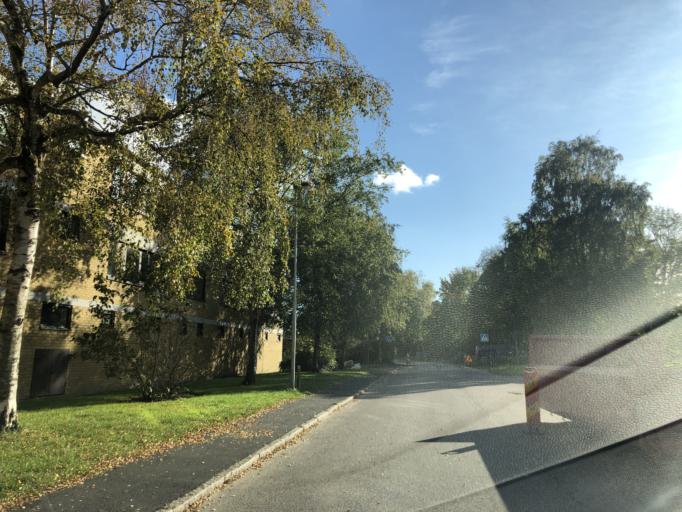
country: SE
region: Vaestra Goetaland
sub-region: Goteborg
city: Majorna
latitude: 57.6308
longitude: 11.9333
